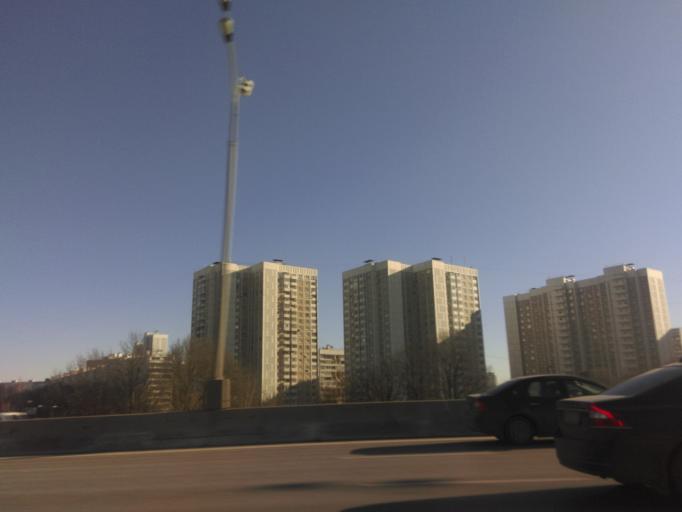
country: RU
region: Moskovskaya
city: Marfino
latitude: 55.7092
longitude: 37.3889
